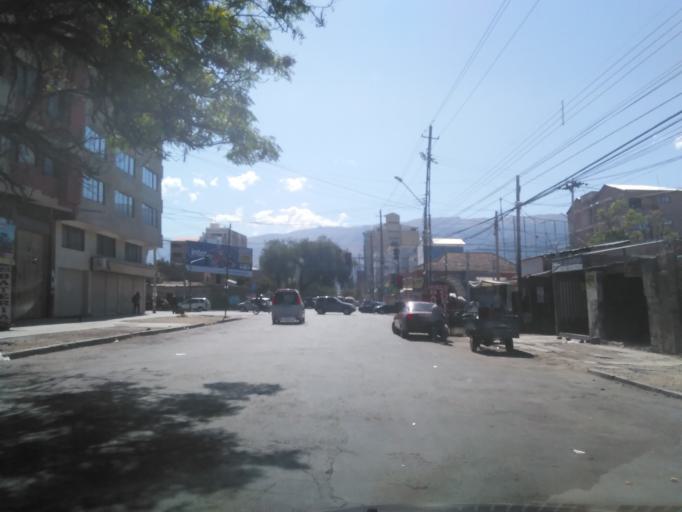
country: BO
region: Cochabamba
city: Cochabamba
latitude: -17.3989
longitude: -66.1483
